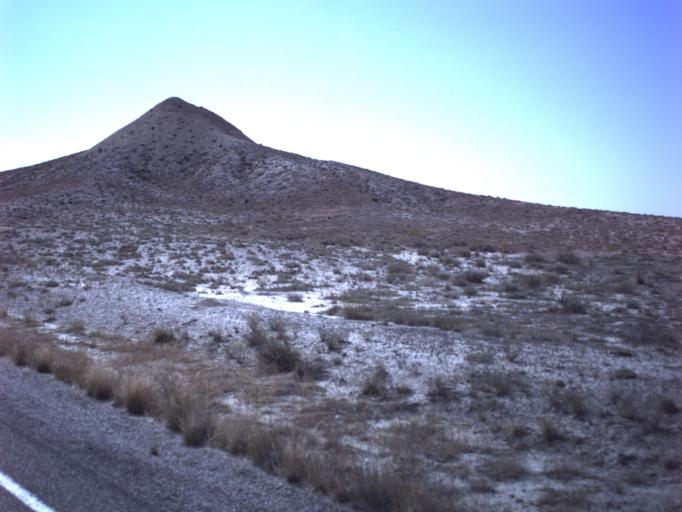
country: US
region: Utah
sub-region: Grand County
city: Moab
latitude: 38.9356
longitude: -109.3463
